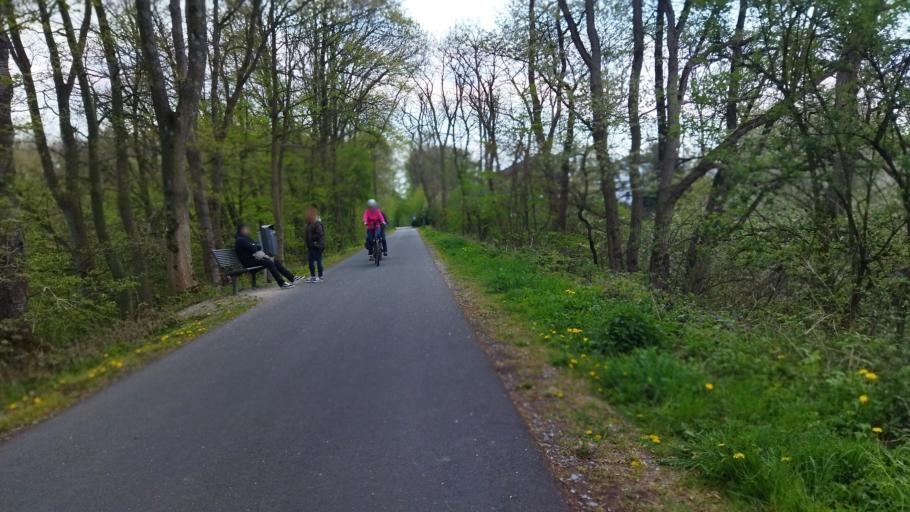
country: DE
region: North Rhine-Westphalia
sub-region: Regierungsbezirk Dusseldorf
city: Heiligenhaus
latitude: 51.3360
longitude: 6.9390
